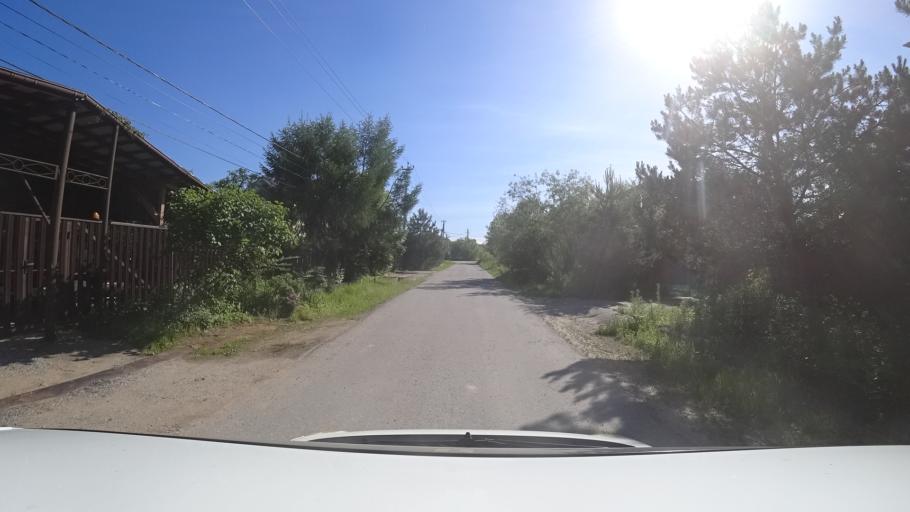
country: RU
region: Khabarovsk Krai
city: Topolevo
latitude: 48.5449
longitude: 135.1796
